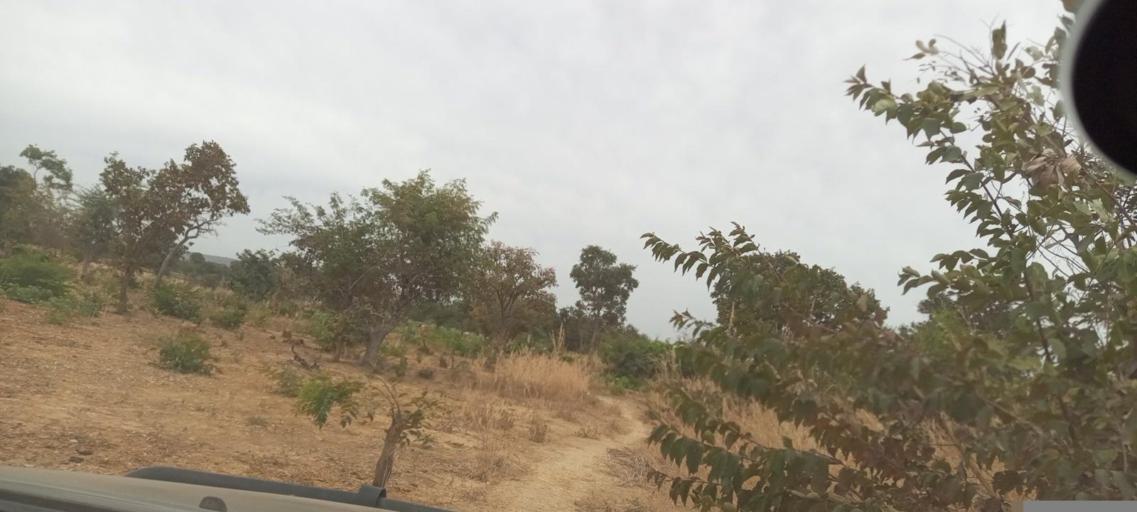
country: ML
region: Koulikoro
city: Kati
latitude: 12.7458
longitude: -8.3516
